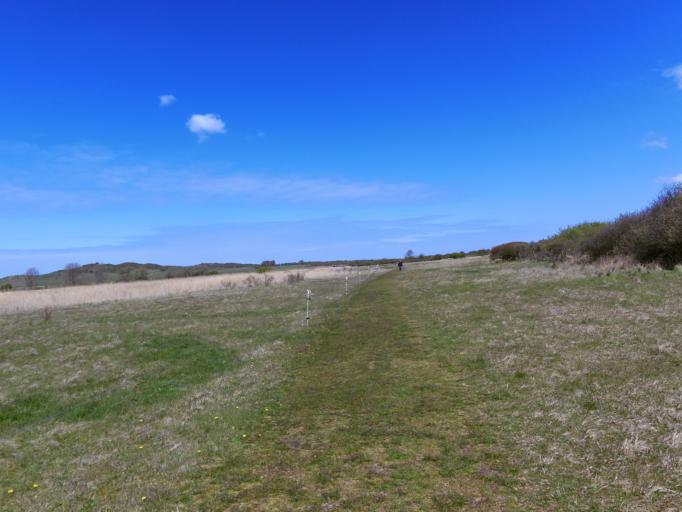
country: DE
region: Mecklenburg-Vorpommern
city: Hiddensee
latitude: 54.5916
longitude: 13.1413
